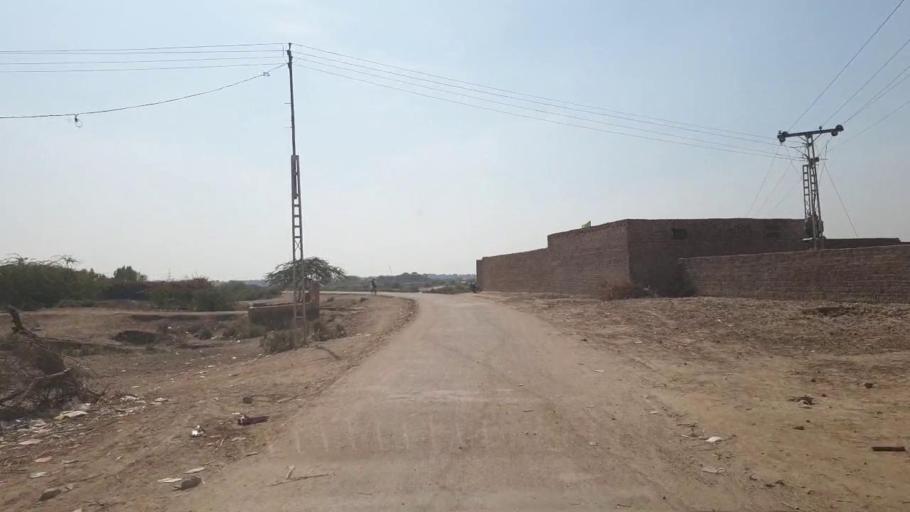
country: PK
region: Sindh
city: Chambar
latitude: 25.3341
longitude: 68.8051
